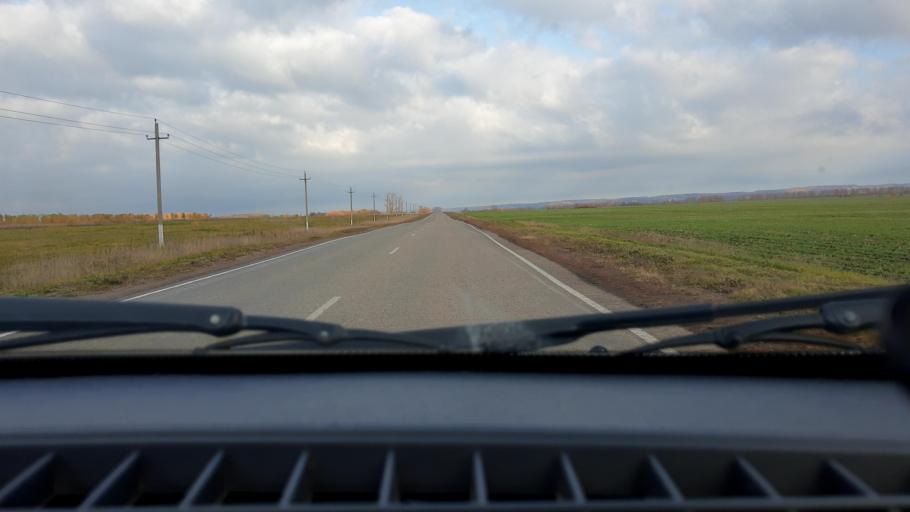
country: RU
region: Bashkortostan
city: Ulukulevo
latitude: 54.4026
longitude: 56.3768
